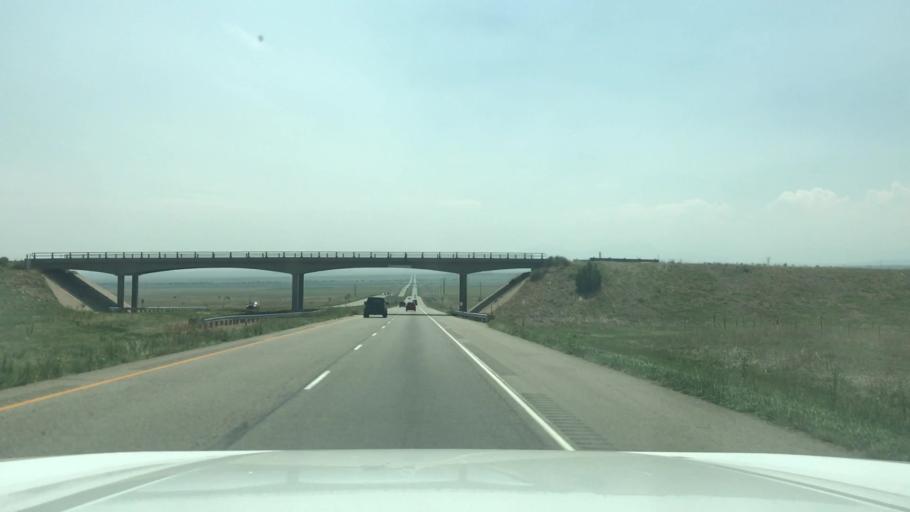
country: US
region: Colorado
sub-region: Pueblo County
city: Colorado City
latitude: 37.8953
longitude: -104.8294
